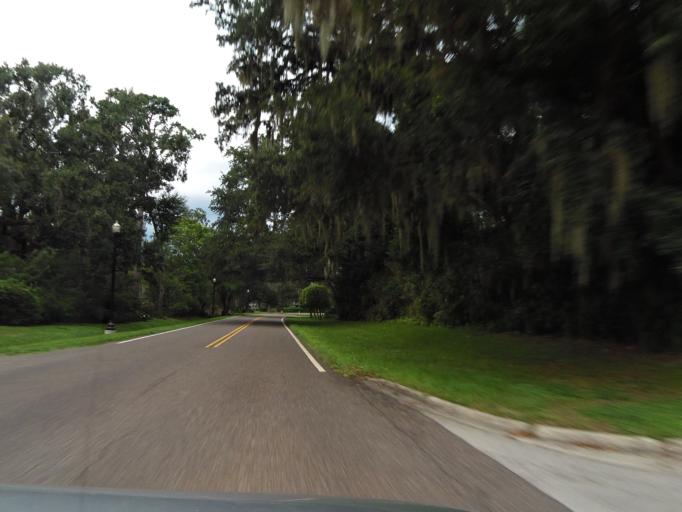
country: US
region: Florida
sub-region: Duval County
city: Jacksonville
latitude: 30.2622
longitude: -81.6986
